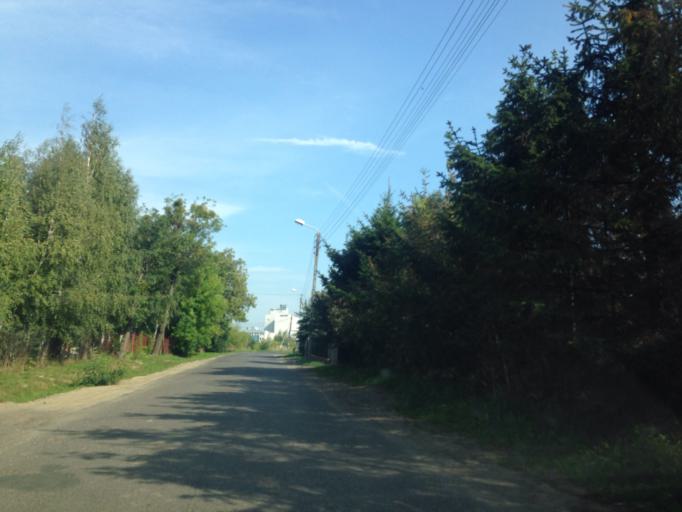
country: PL
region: Kujawsko-Pomorskie
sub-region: Powiat golubsko-dobrzynski
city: Golub-Dobrzyn
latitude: 53.1188
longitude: 19.0424
